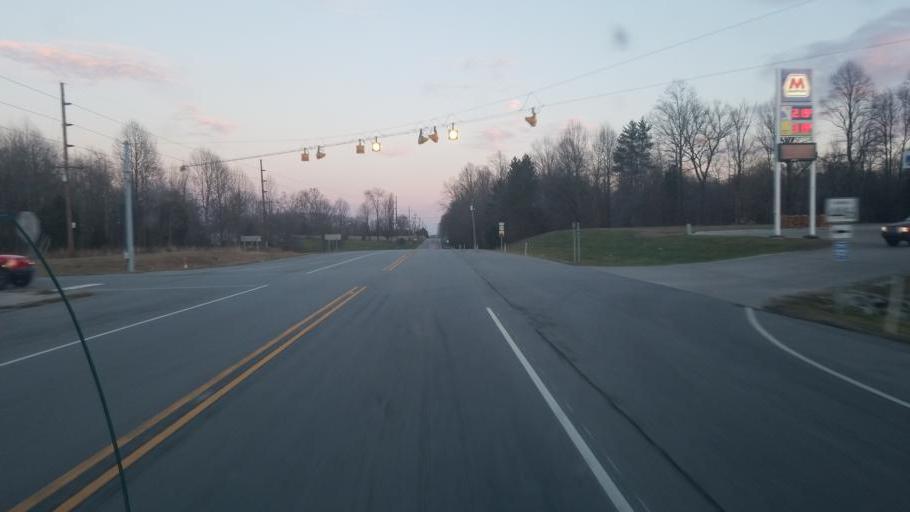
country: US
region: Indiana
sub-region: Lawrence County
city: Bedford
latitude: 38.8746
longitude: -86.3399
